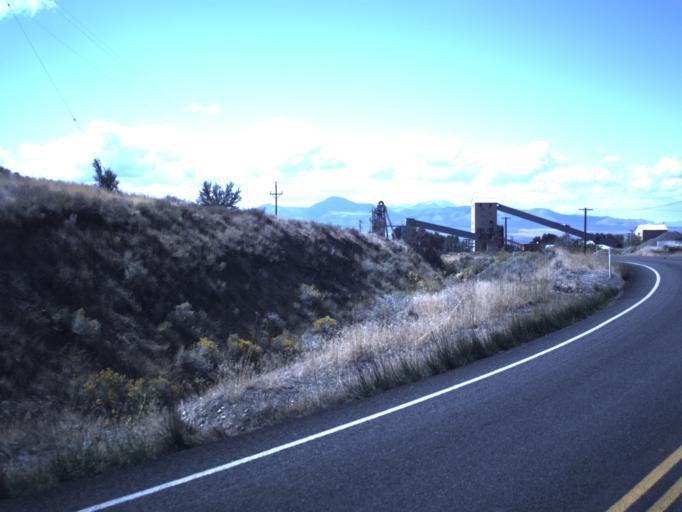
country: US
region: Utah
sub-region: Utah County
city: Santaquin
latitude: 40.0049
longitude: -111.8072
